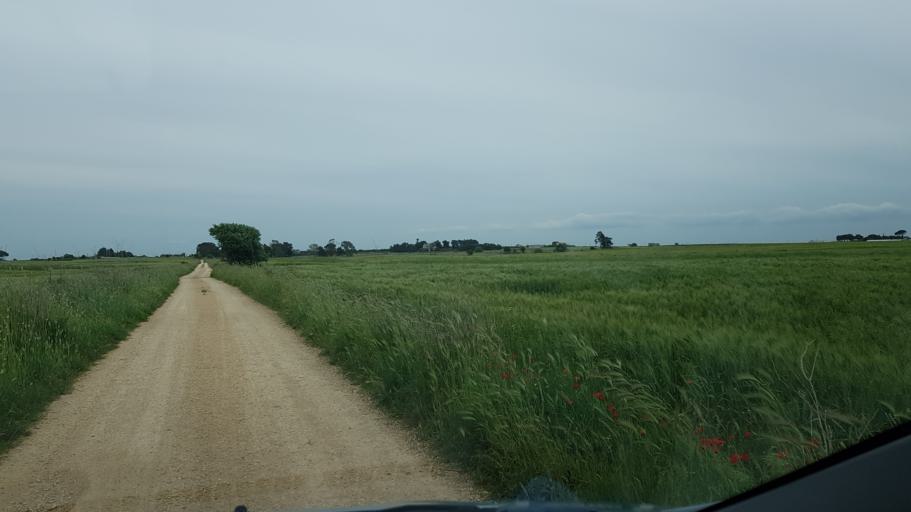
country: IT
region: Apulia
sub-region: Provincia di Brindisi
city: Brindisi
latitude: 40.6558
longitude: 17.8816
